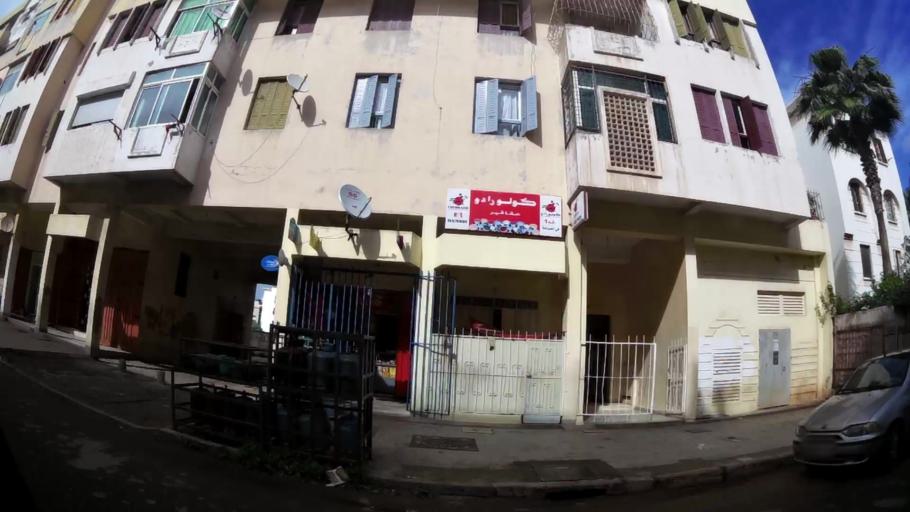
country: MA
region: Grand Casablanca
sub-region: Mohammedia
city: Mohammedia
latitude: 33.6761
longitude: -7.3837
